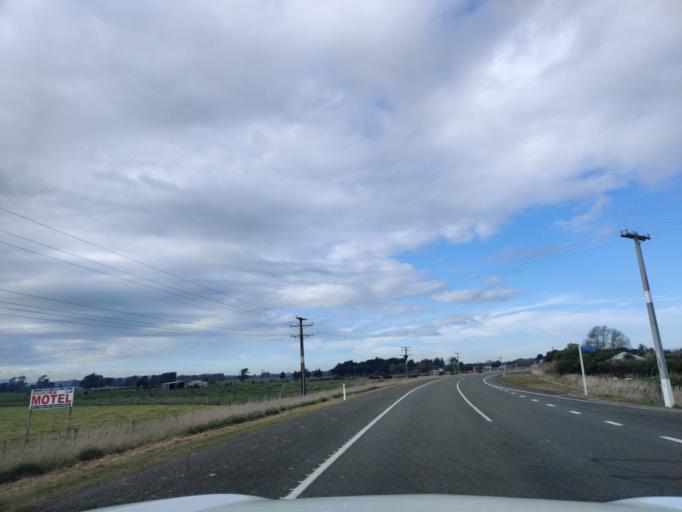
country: NZ
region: Manawatu-Wanganui
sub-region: Palmerston North City
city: Palmerston North
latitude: -40.3333
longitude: 175.8462
